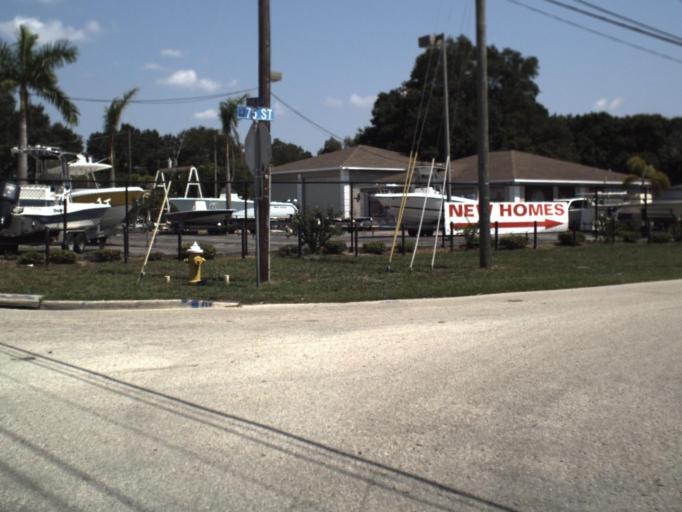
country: US
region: Florida
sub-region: Pinellas County
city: Kenneth City
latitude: 27.8391
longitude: -82.7421
